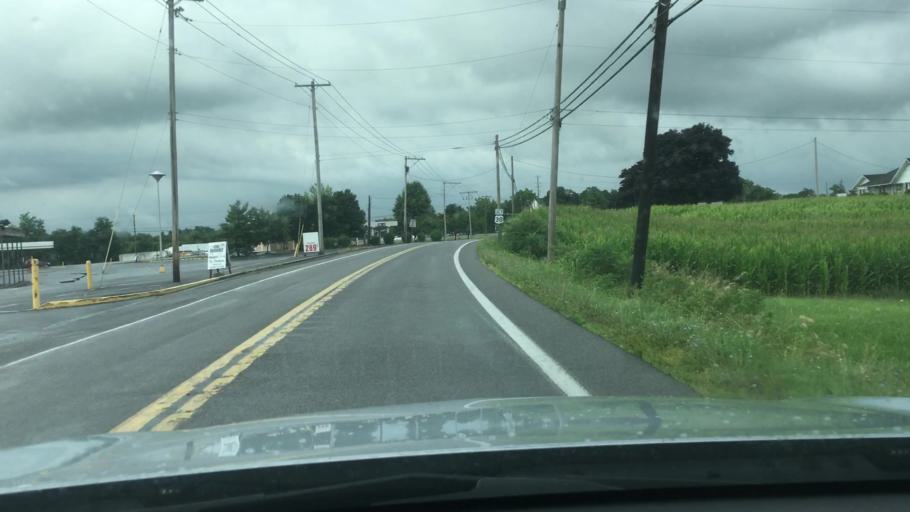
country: US
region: Pennsylvania
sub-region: Franklin County
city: Chambersburg
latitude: 39.9320
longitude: -77.6960
